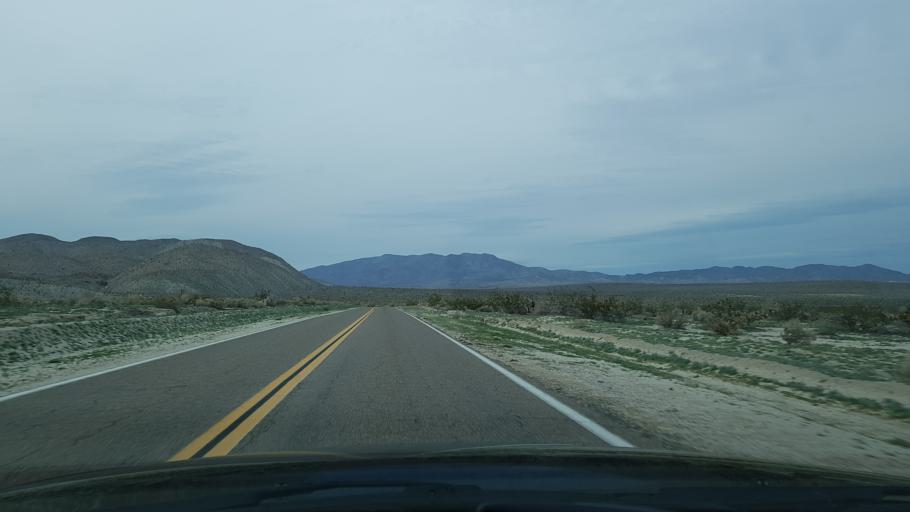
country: US
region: California
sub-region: San Diego County
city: Pine Valley
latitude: 32.8544
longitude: -116.2052
